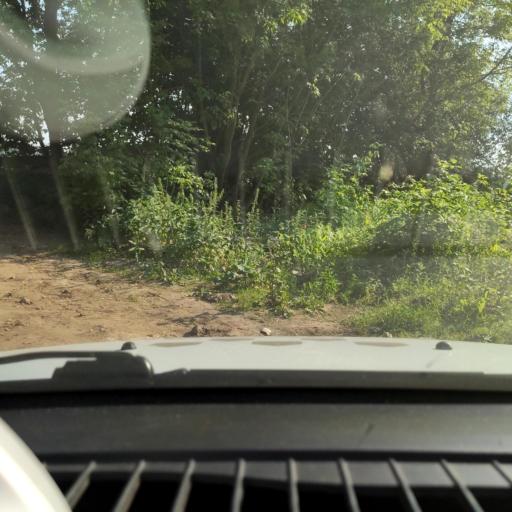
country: RU
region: Perm
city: Perm
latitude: 58.0233
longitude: 56.2110
